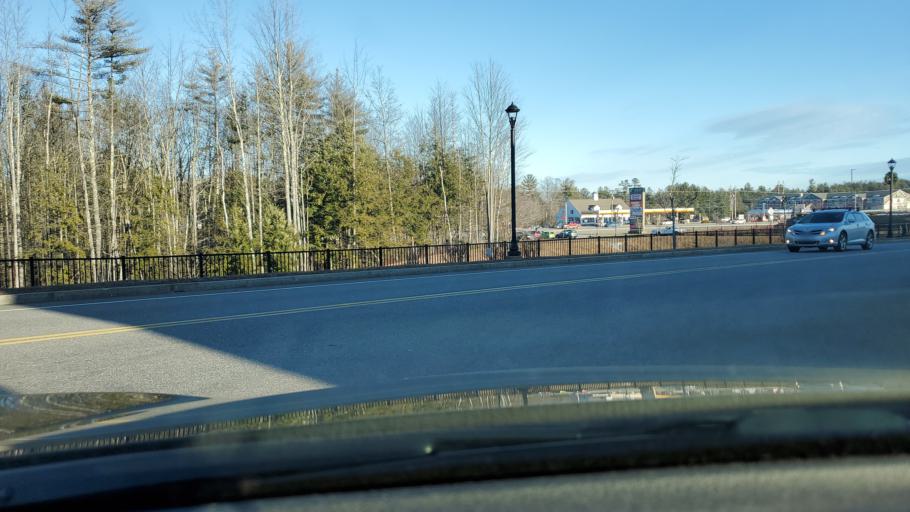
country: US
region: New Hampshire
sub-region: Strafford County
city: Rochester
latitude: 43.3341
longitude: -71.0106
